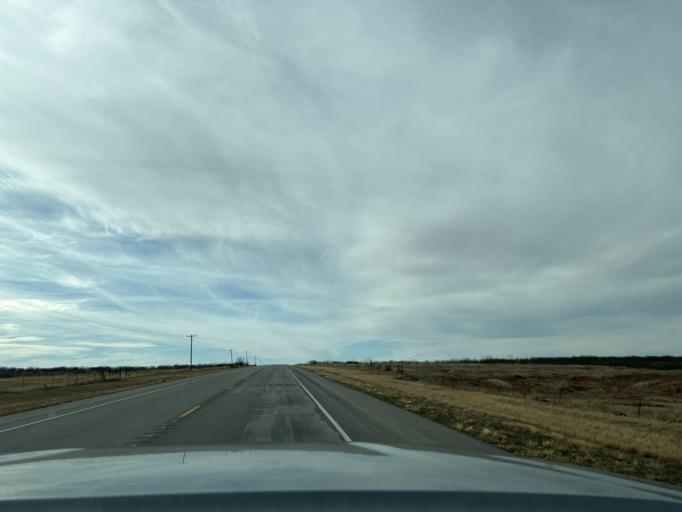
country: US
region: Texas
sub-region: Jones County
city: Anson
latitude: 32.7504
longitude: -99.6644
